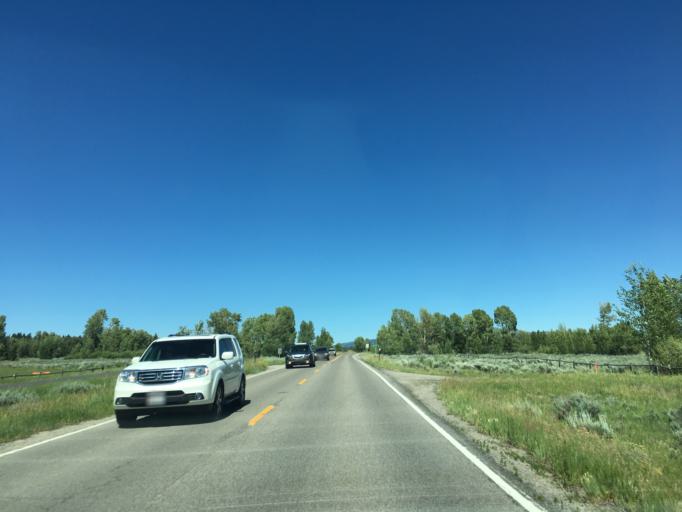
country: US
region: Wyoming
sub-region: Teton County
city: Moose Wilson Road
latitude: 43.5945
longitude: -110.8086
